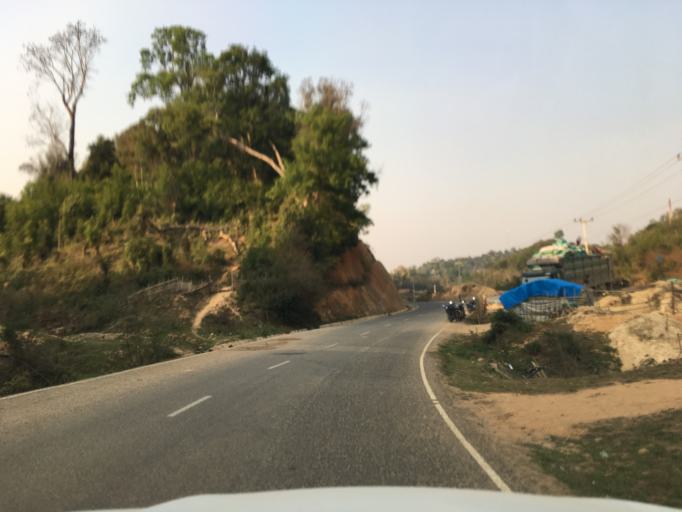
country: LA
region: Houaphan
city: Xam Nua
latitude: 20.5980
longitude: 104.0683
